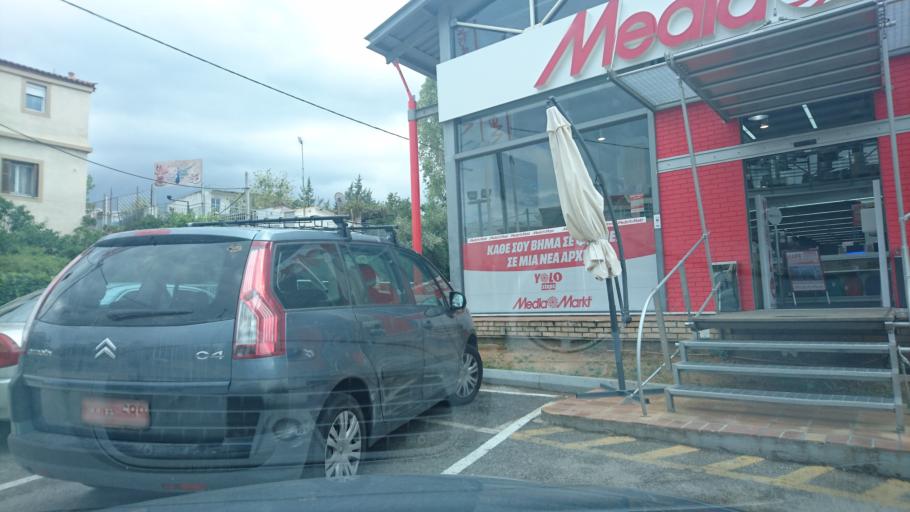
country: GR
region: Attica
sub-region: Nomarchia Athinas
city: Agia Paraskevi
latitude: 38.0142
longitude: 23.8183
